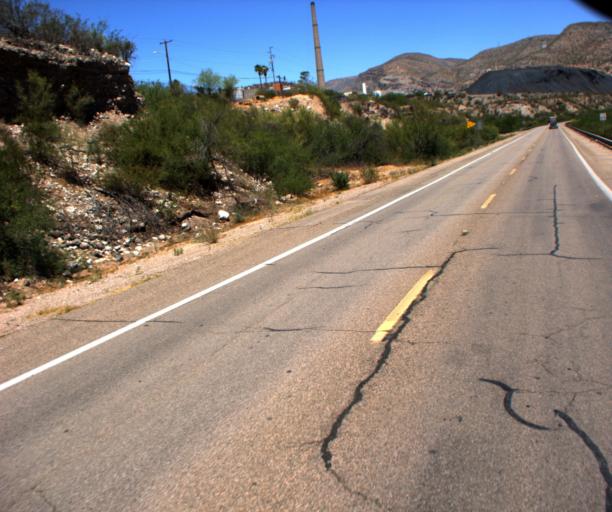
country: US
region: Arizona
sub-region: Pinal County
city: Kearny
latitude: 32.9912
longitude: -110.7697
